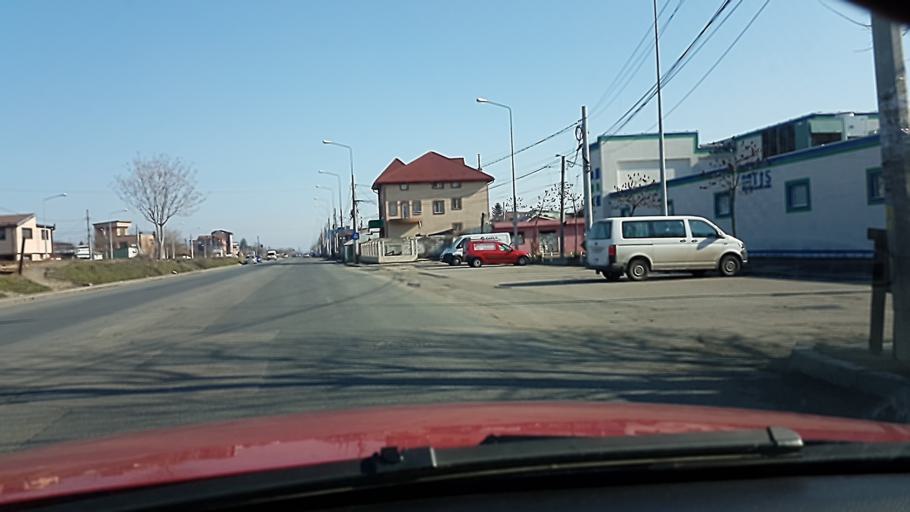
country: RO
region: Ilfov
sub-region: Comuna Pantelimon
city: Pantelimon
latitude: 44.4311
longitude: 26.1966
